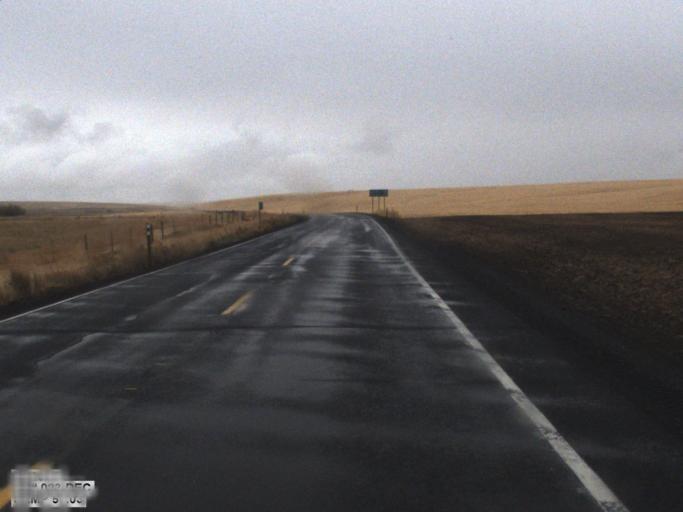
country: US
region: Washington
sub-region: Lincoln County
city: Davenport
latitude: 47.4035
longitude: -118.1673
